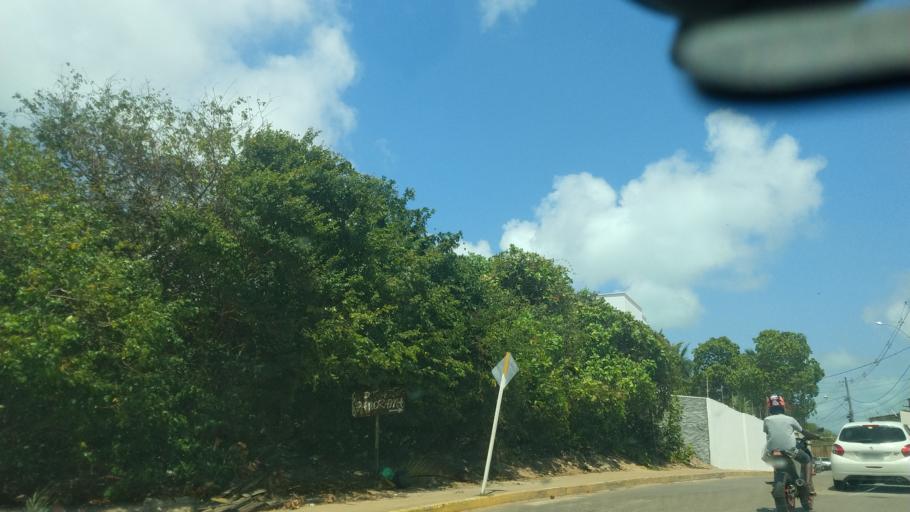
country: BR
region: Rio Grande do Norte
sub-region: Ares
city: Ares
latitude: -6.2343
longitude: -35.0495
